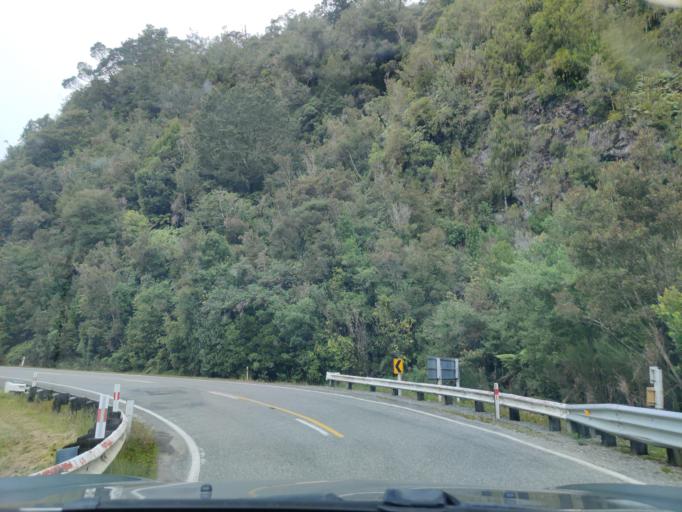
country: NZ
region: West Coast
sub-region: Buller District
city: Westport
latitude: -41.8500
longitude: 171.7314
